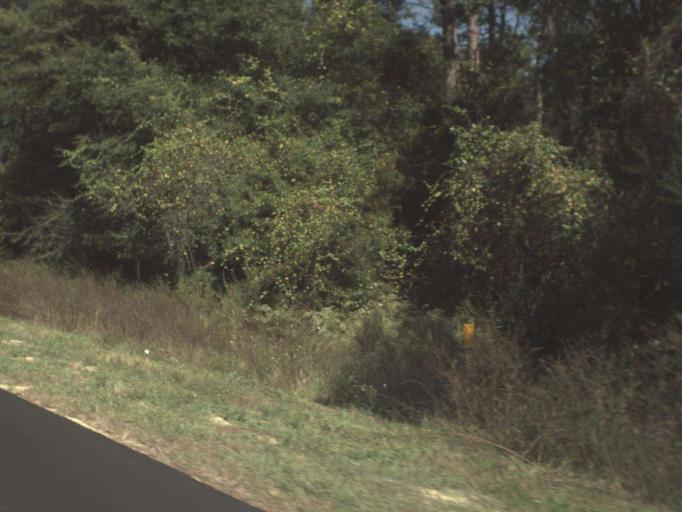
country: US
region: Florida
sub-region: Walton County
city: DeFuniak Springs
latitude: 30.7666
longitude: -86.1545
